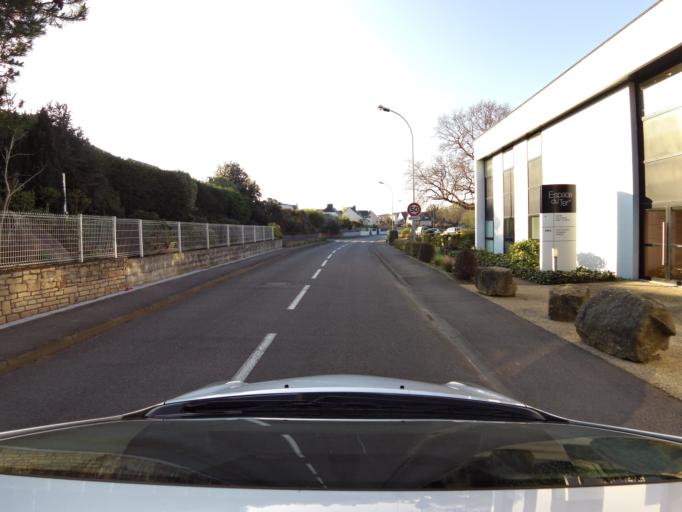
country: FR
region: Brittany
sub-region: Departement du Morbihan
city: Larmor-Plage
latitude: 47.7283
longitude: -3.3864
